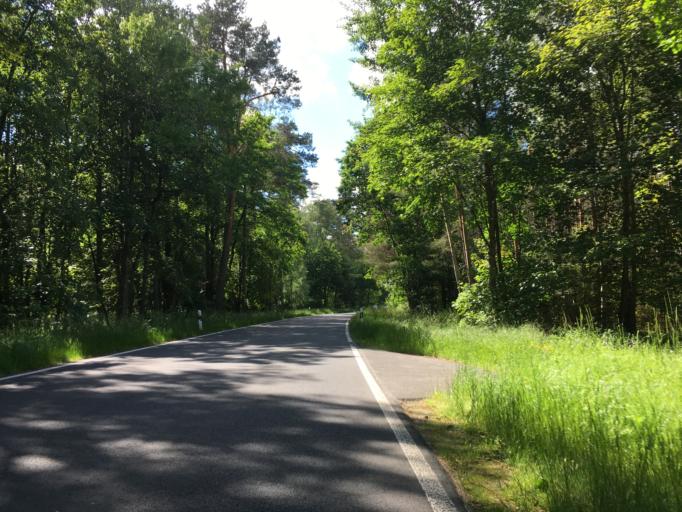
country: DE
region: Brandenburg
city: Protzel
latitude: 52.6008
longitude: 13.9980
